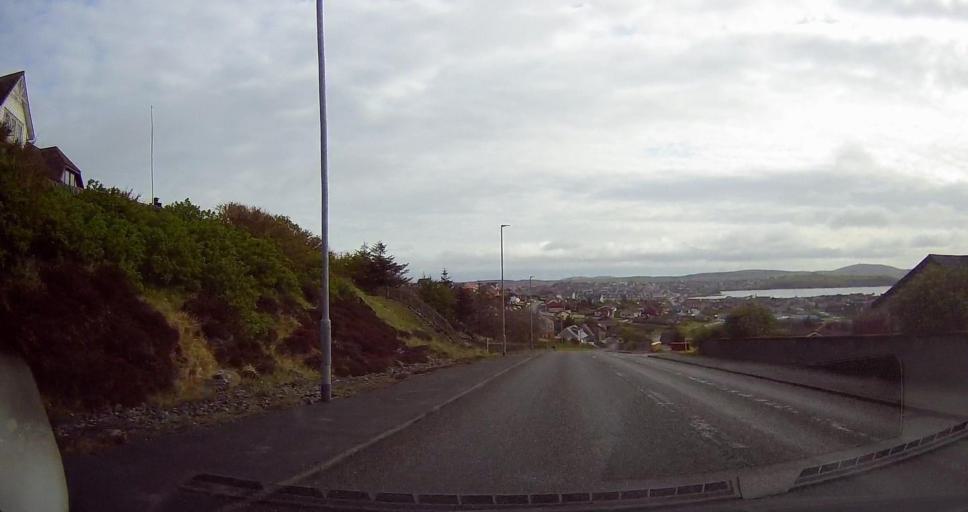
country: GB
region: Scotland
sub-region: Shetland Islands
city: Lerwick
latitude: 60.1424
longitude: -1.1823
